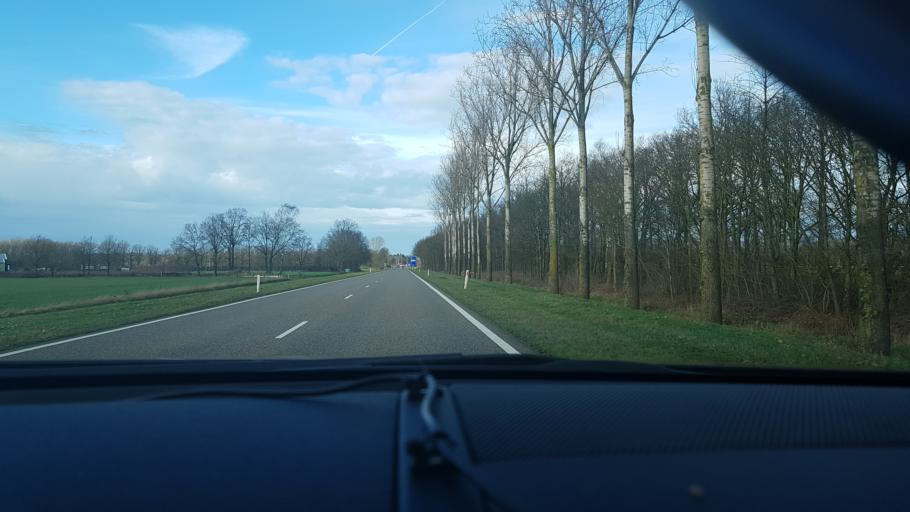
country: NL
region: Limburg
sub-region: Gemeente Peel en Maas
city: Maasbree
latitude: 51.3463
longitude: 6.0212
